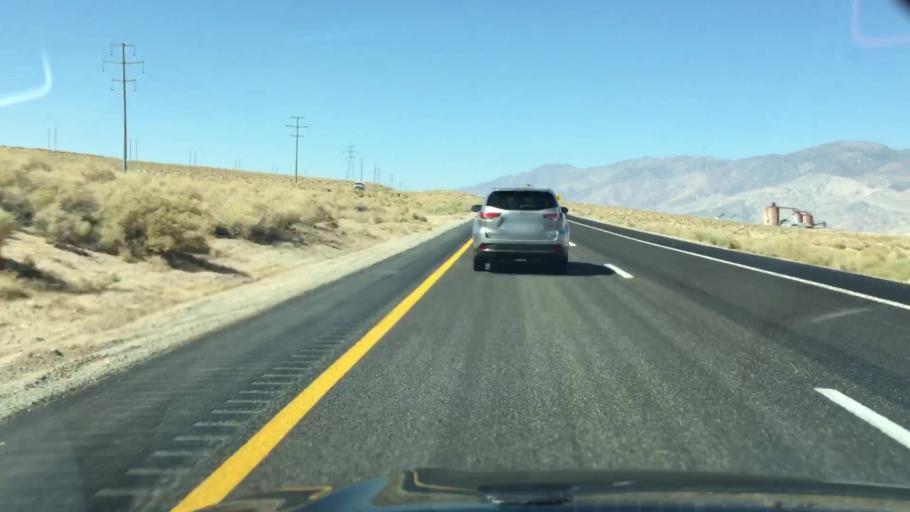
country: US
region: California
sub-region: Inyo County
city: Lone Pine
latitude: 36.4670
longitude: -118.0362
